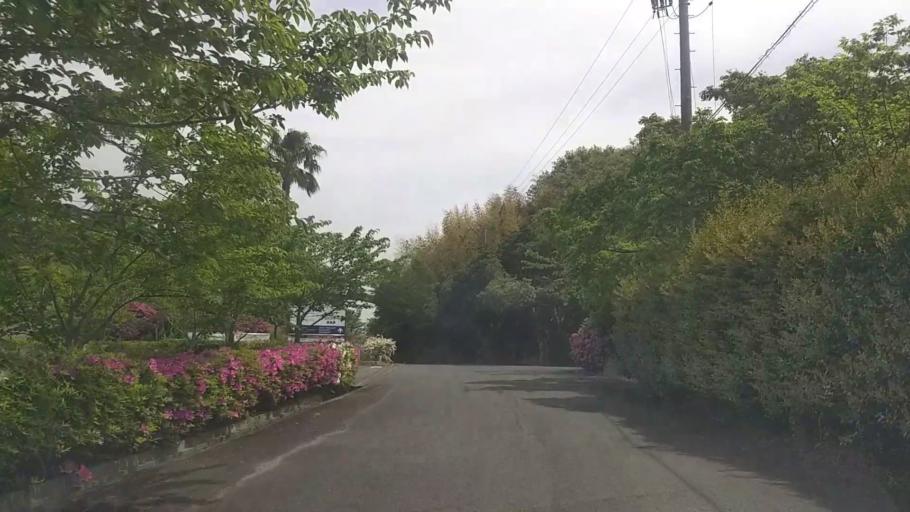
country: JP
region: Shizuoka
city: Kosai-shi
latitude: 34.7535
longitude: 137.5193
